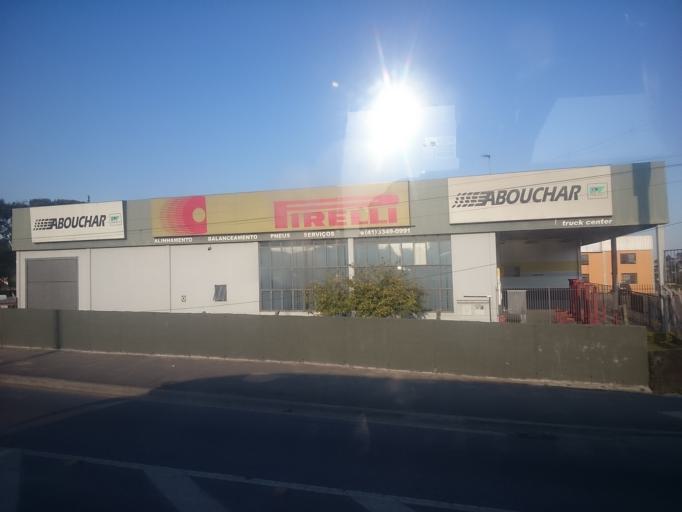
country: BR
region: Parana
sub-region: Sao Jose Dos Pinhais
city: Sao Jose dos Pinhais
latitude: -25.5233
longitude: -49.2953
